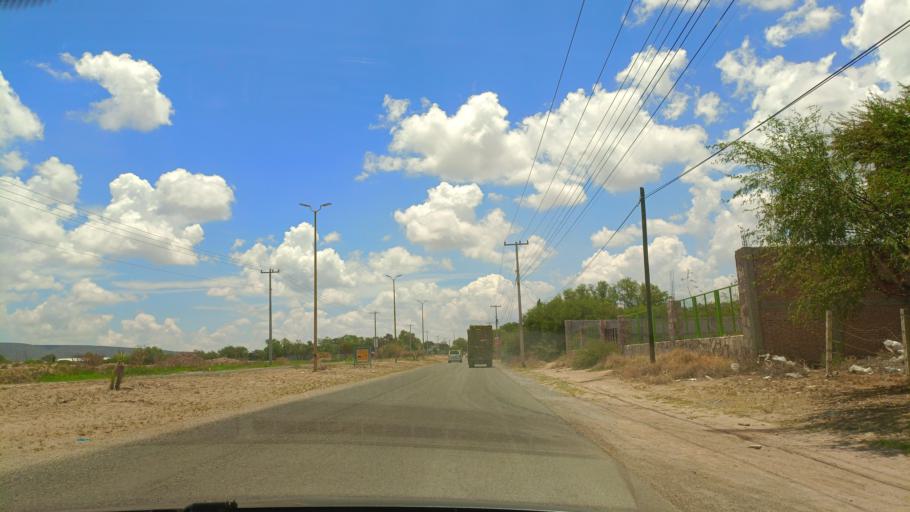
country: MX
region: Guanajuato
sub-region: San Luis de la Paz
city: San Ignacio
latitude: 21.2876
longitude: -100.5474
